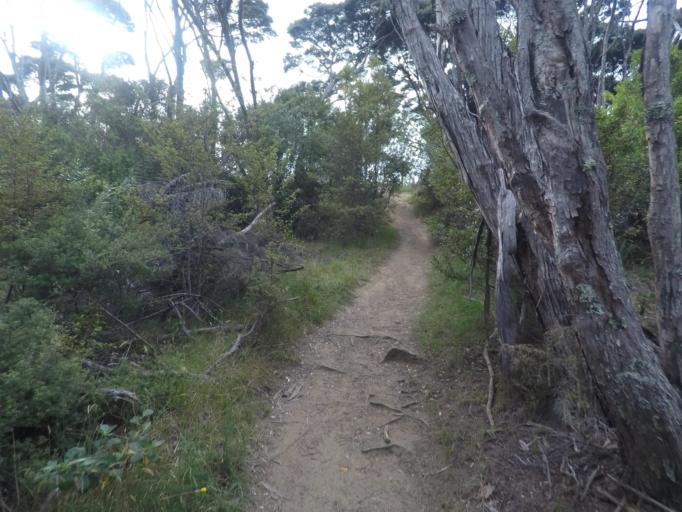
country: NZ
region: Auckland
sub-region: Auckland
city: Parakai
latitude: -36.5156
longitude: 174.2433
